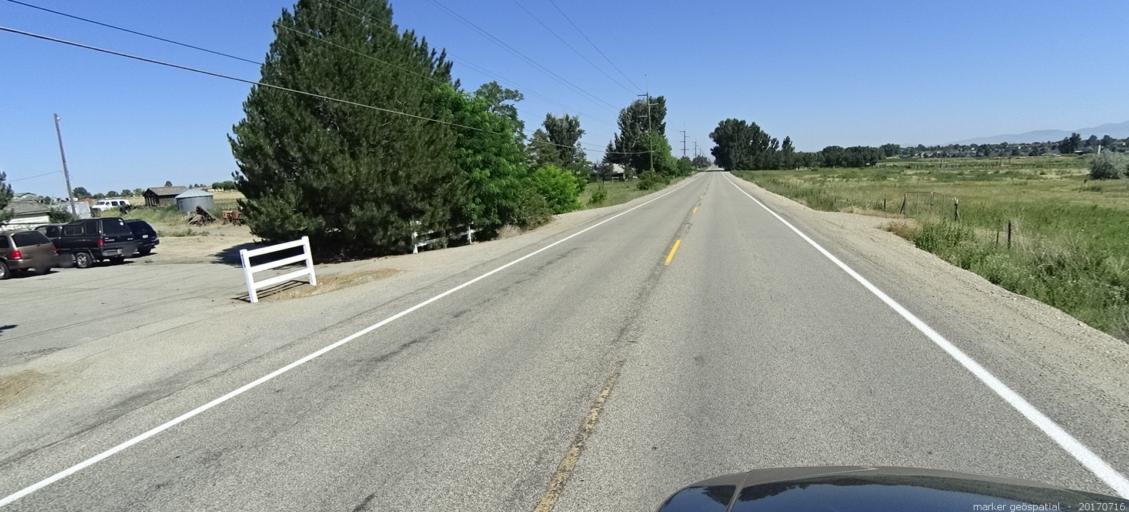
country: US
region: Idaho
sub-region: Ada County
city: Kuna
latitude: 43.5200
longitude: -116.3345
